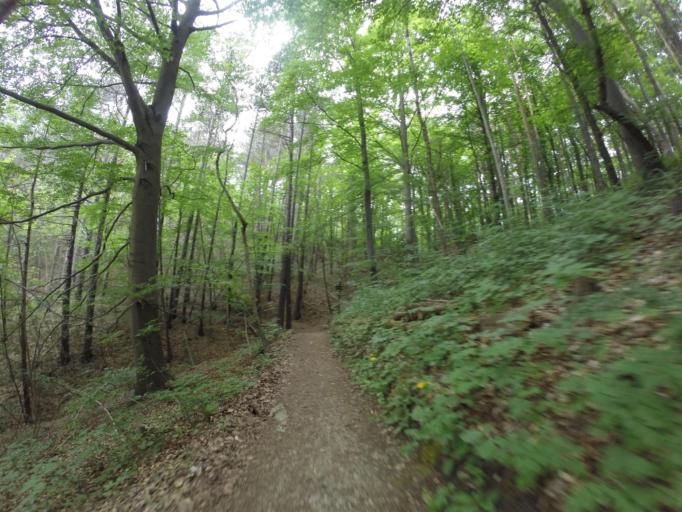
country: DE
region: Thuringia
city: Sulza
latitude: 50.8961
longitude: 11.6225
